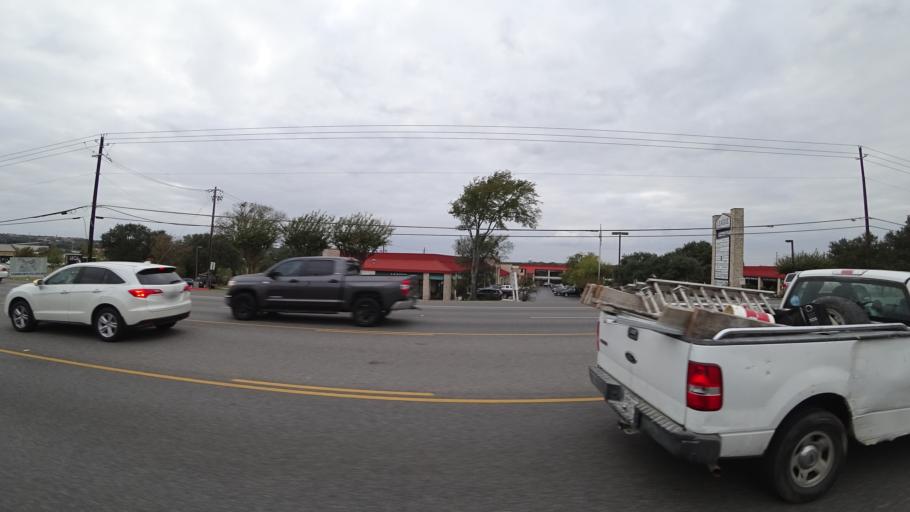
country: US
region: Texas
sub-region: Travis County
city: The Hills
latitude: 30.3492
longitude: -97.9636
